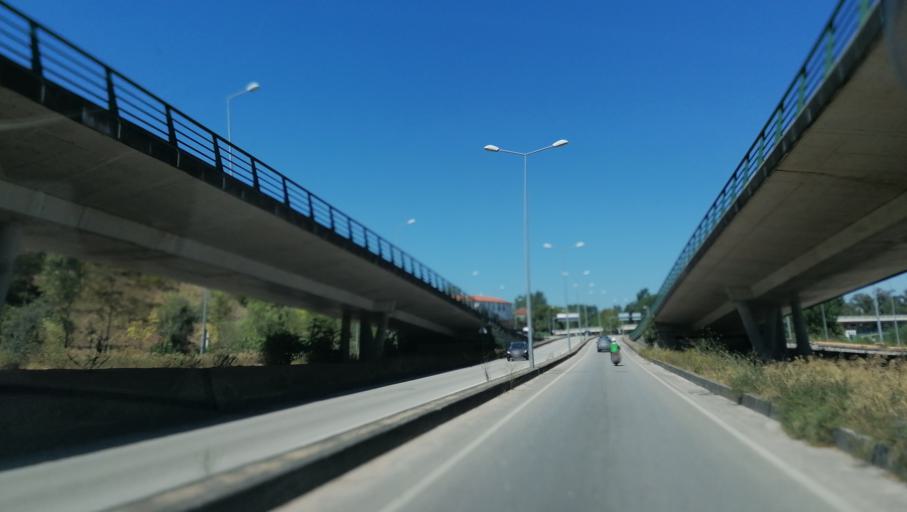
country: PT
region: Coimbra
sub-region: Coimbra
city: Coimbra
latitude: 40.2121
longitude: -8.4405
